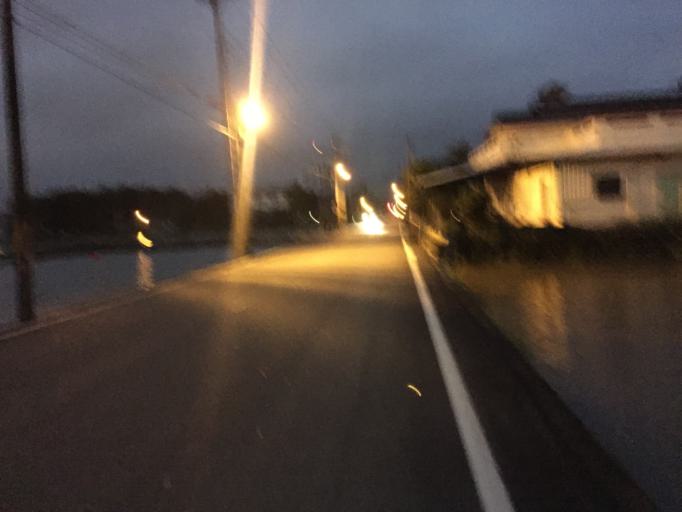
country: TW
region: Taiwan
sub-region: Yilan
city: Yilan
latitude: 24.6577
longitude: 121.7853
